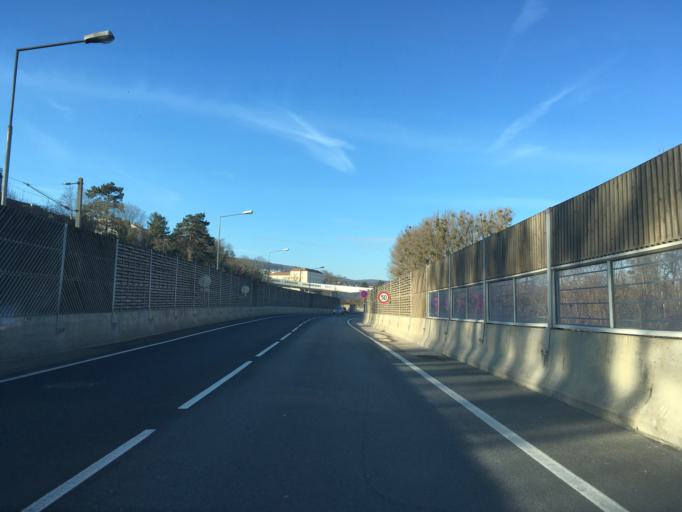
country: AT
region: Lower Austria
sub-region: Politischer Bezirk Wien-Umgebung
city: Klosterneuburg
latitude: 48.3144
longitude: 16.3204
